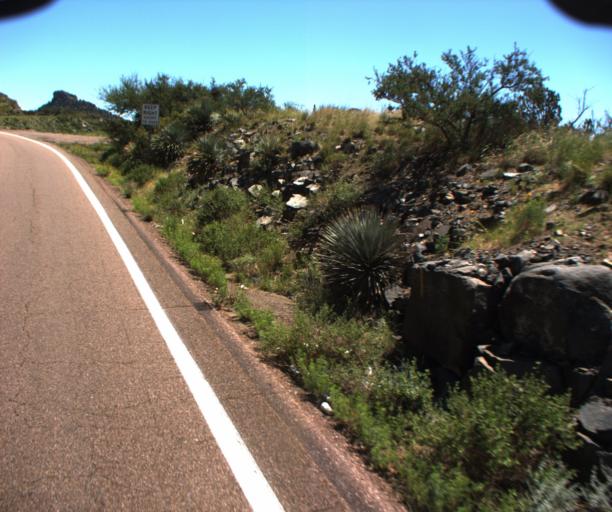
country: US
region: Arizona
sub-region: Navajo County
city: Cibecue
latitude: 33.8039
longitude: -110.4800
